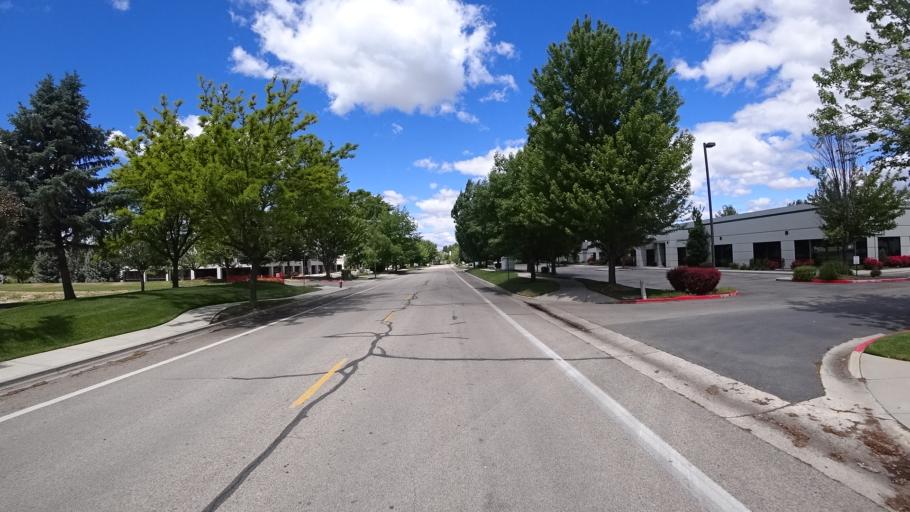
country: US
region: Idaho
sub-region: Ada County
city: Eagle
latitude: 43.6602
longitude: -116.3411
